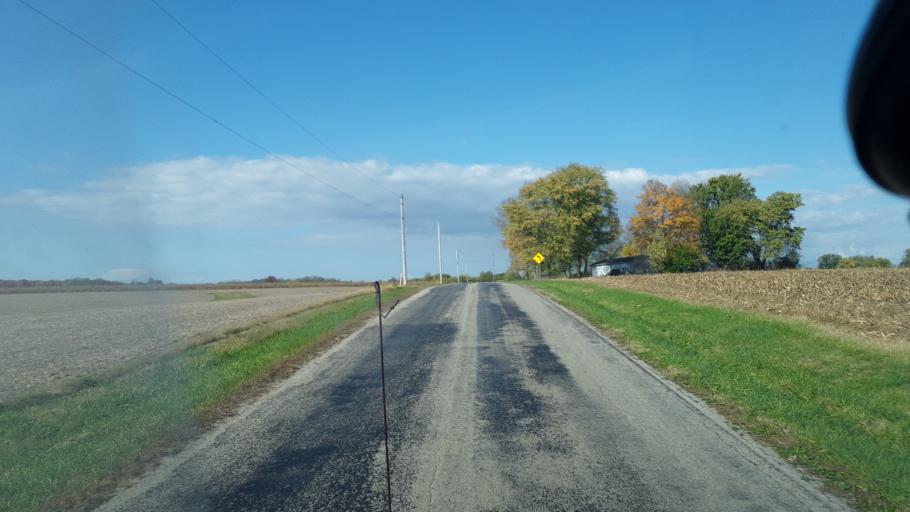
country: US
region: Ohio
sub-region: Highland County
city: Leesburg
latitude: 39.2825
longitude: -83.5823
